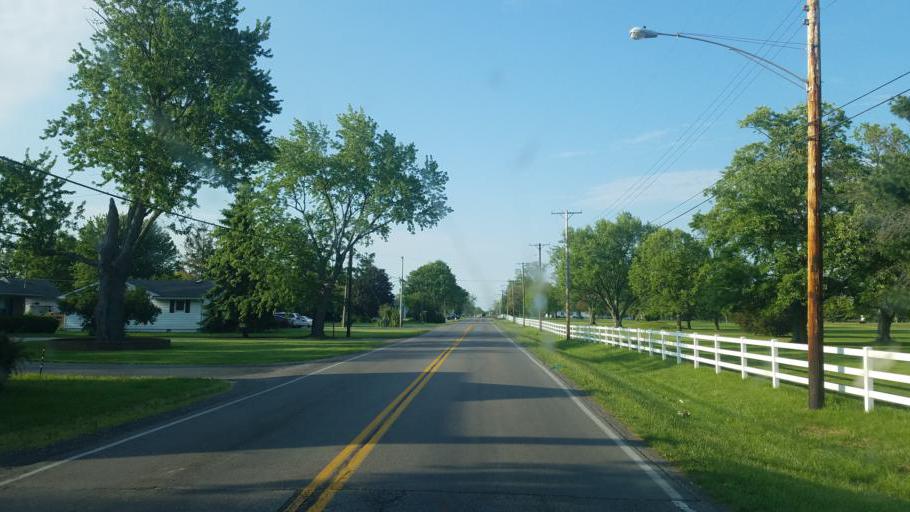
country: US
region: Ohio
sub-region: Fayette County
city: Washington Court House
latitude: 39.5284
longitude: -83.4432
